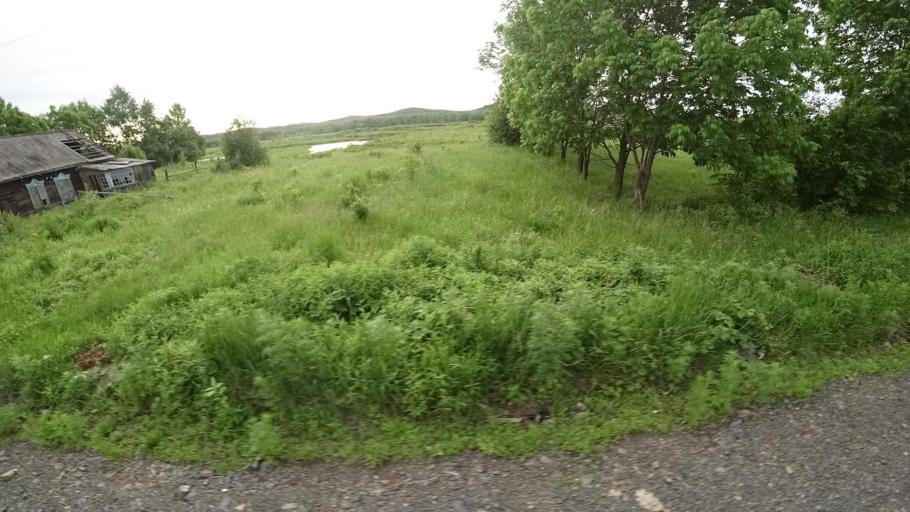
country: RU
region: Khabarovsk Krai
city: Amursk
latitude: 49.8889
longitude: 136.1293
